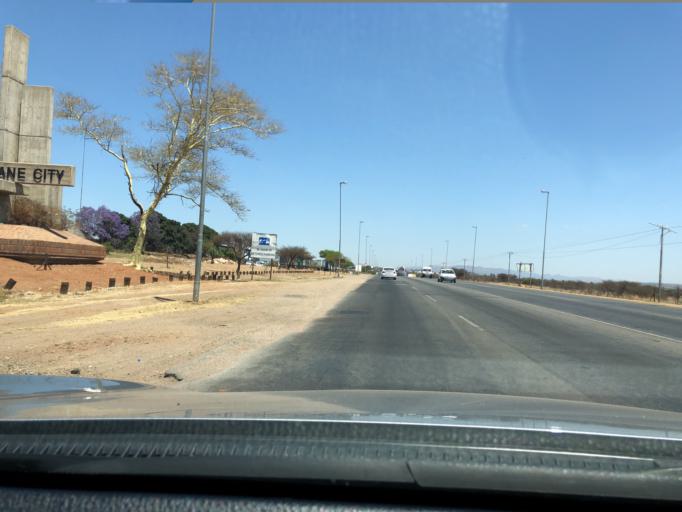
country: ZA
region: Limpopo
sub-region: Capricorn District Municipality
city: Polokwane
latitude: -23.8620
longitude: 29.4705
